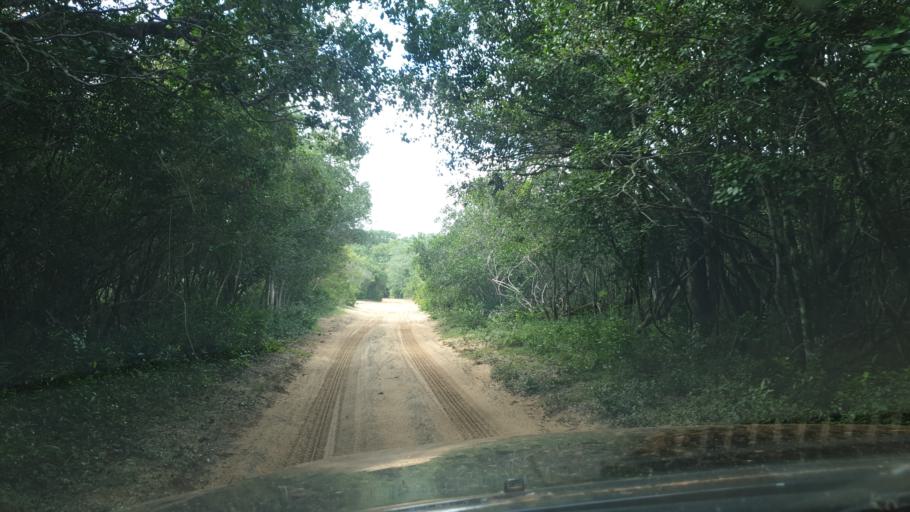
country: LK
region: North Central
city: Anuradhapura
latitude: 8.4193
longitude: 80.0162
